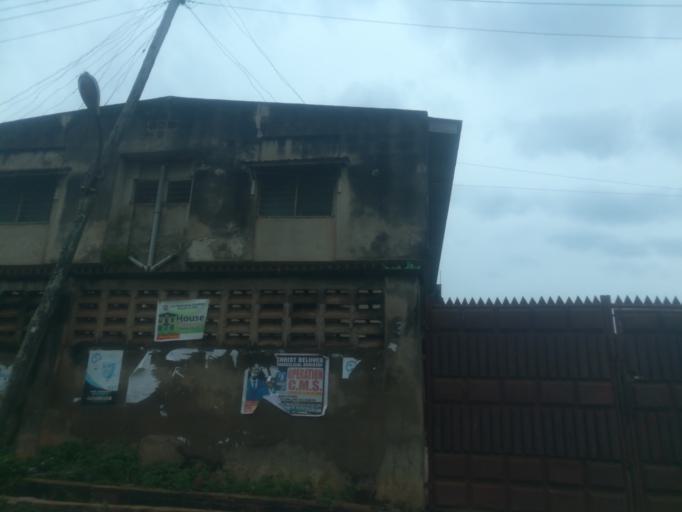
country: NG
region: Oyo
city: Egbeda
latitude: 7.4054
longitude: 3.9780
